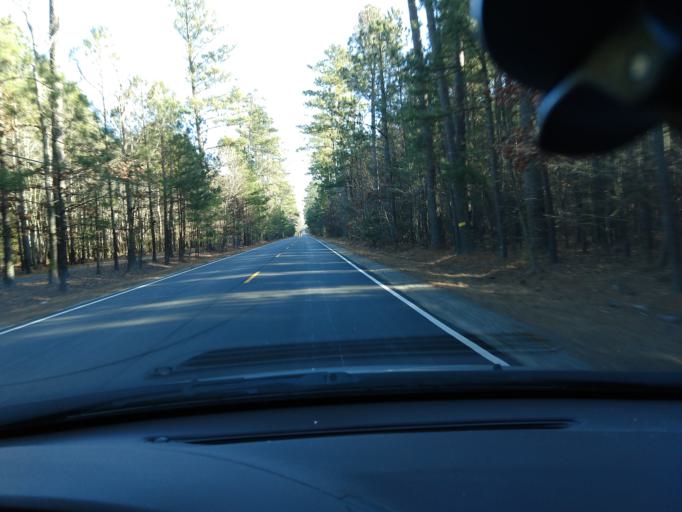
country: US
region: Virginia
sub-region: Surry County
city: Surry
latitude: 37.2802
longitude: -76.9160
